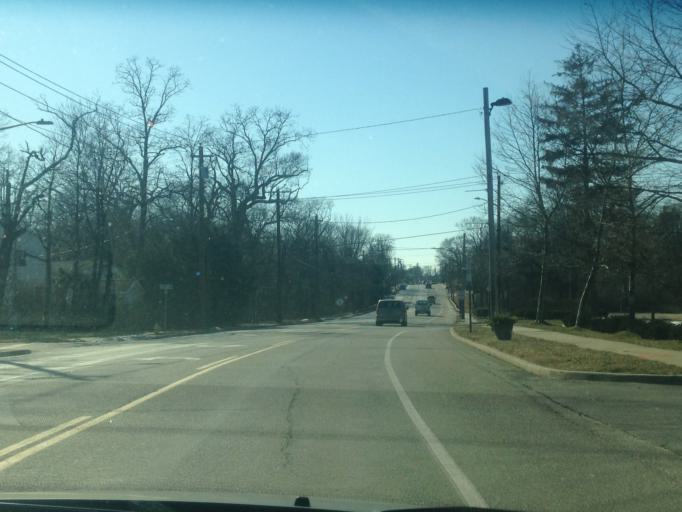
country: US
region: New York
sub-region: Suffolk County
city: Blue Point
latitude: 40.7569
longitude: -73.0343
